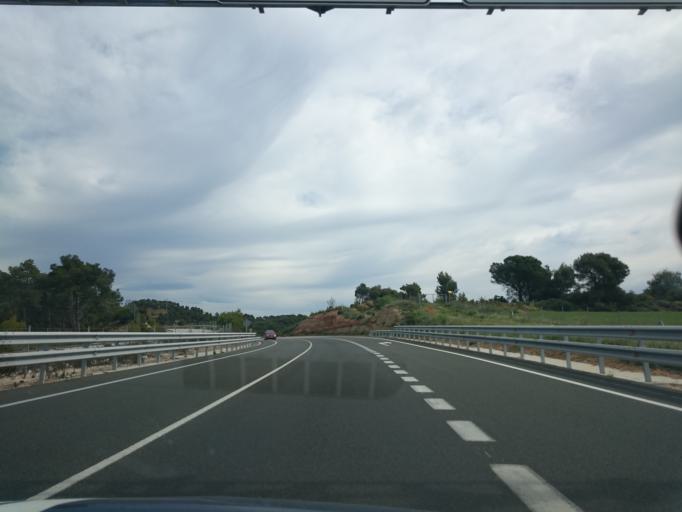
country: ES
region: Catalonia
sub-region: Provincia de Barcelona
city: Castelloli
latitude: 41.6291
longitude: 1.6896
